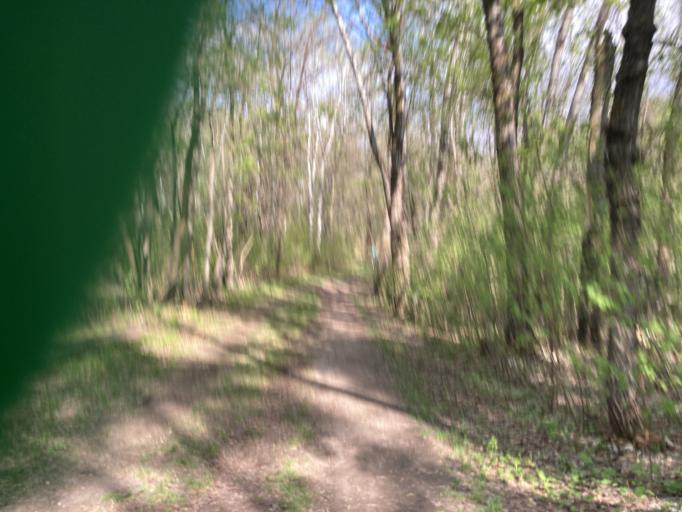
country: CA
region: Manitoba
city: Brandon
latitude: 49.7176
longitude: -99.9036
